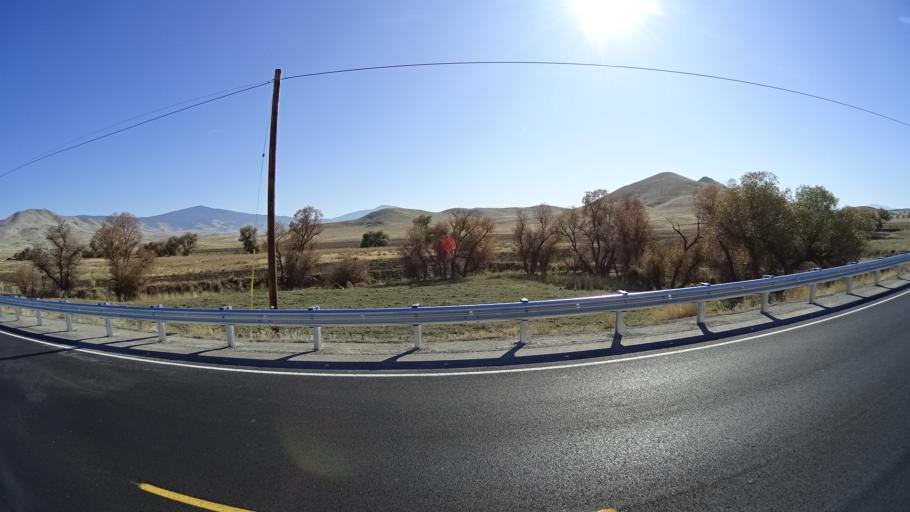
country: US
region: California
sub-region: Siskiyou County
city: Montague
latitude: 41.8400
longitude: -122.4800
